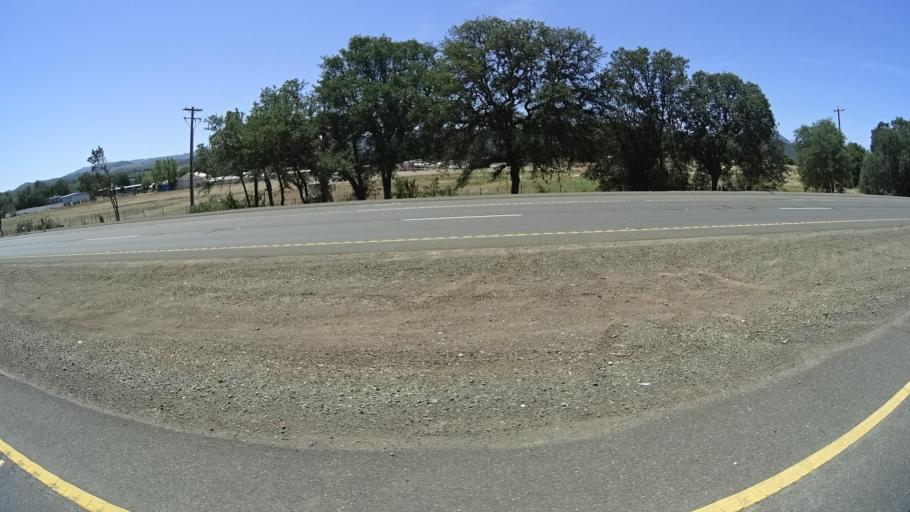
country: US
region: California
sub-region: Lake County
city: Clearlake
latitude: 38.9343
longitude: -122.6209
